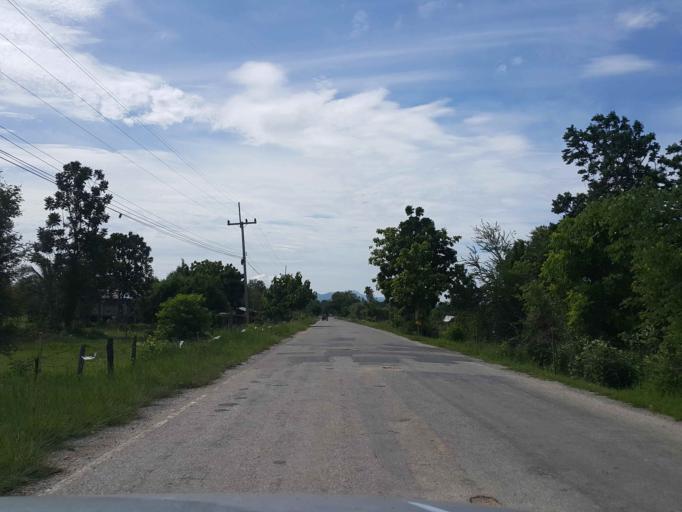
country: TH
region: Sukhothai
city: Ban Dan Lan Hoi
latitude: 17.1233
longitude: 99.5318
